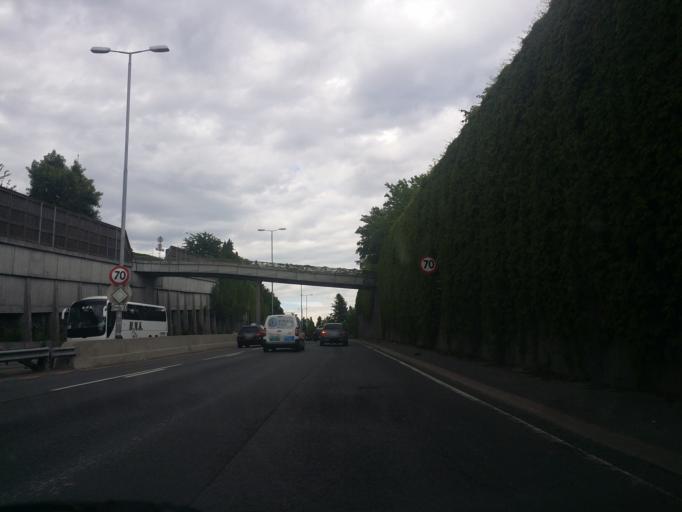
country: NO
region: Oslo
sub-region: Oslo
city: Sjolyststranda
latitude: 59.9398
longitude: 10.6908
